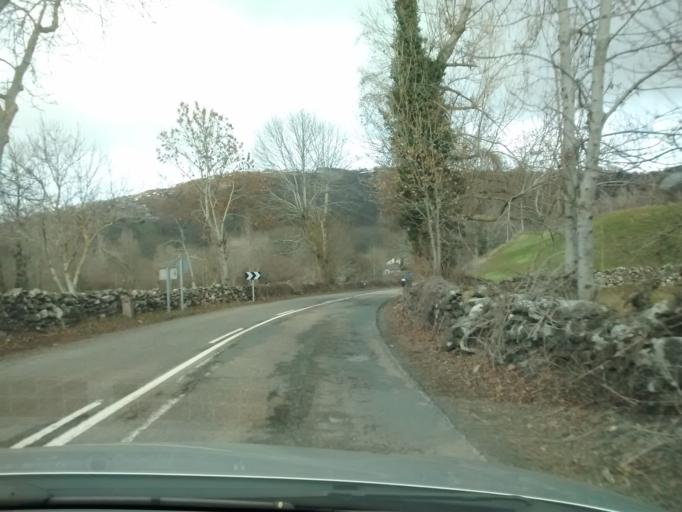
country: ES
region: Castille and Leon
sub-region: Provincia de Burgos
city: Espinosa de los Monteros
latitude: 43.1148
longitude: -3.5816
